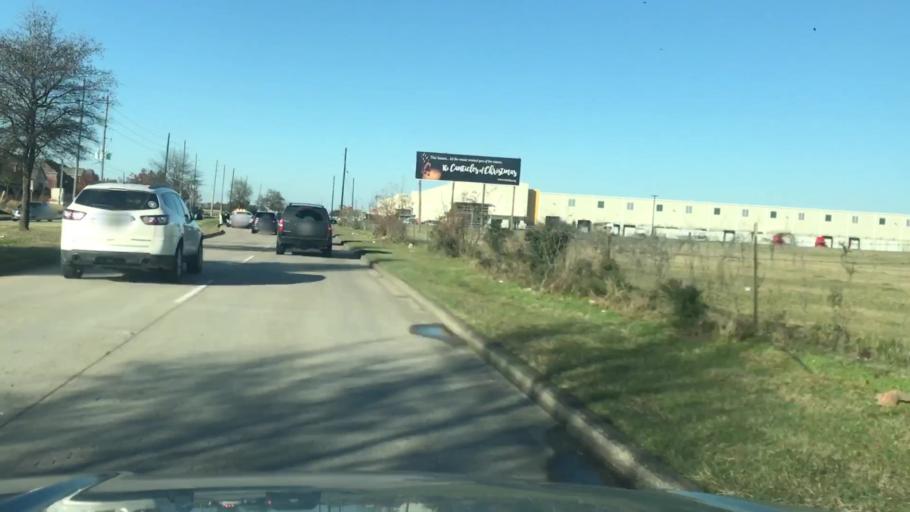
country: US
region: Texas
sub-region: Fort Bend County
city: Cinco Ranch
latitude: 29.8042
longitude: -95.7519
